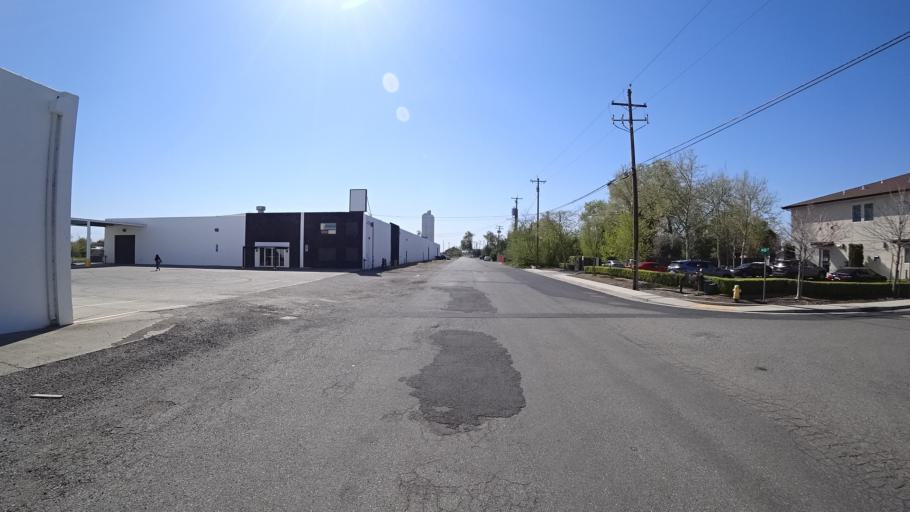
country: US
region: California
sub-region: Glenn County
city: Hamilton City
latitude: 39.7418
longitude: -122.0111
